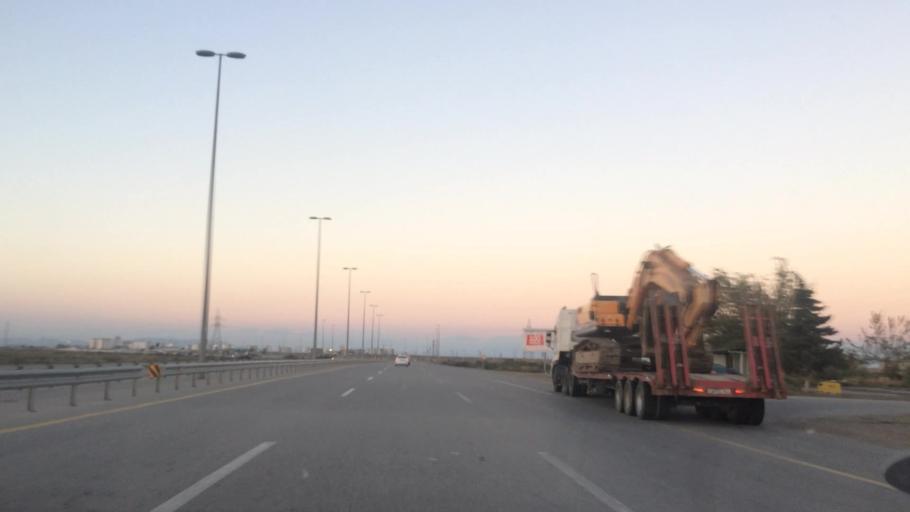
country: AZ
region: Baki
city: Qobustan
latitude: 39.9878
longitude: 49.4278
